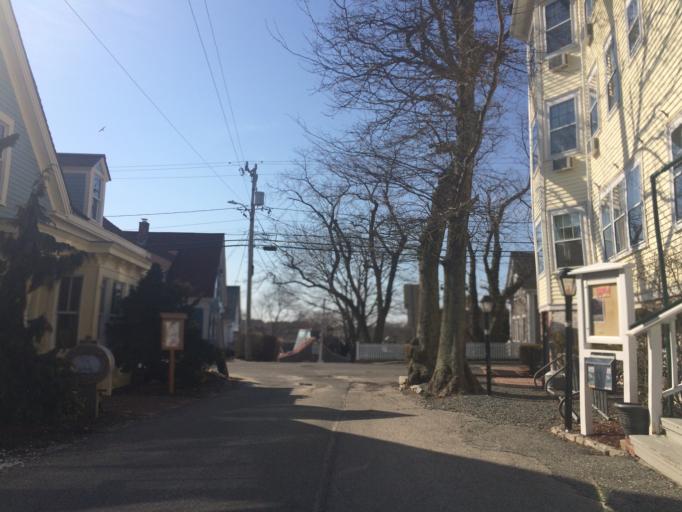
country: US
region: Massachusetts
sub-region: Barnstable County
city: Provincetown
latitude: 42.0494
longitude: -70.1900
